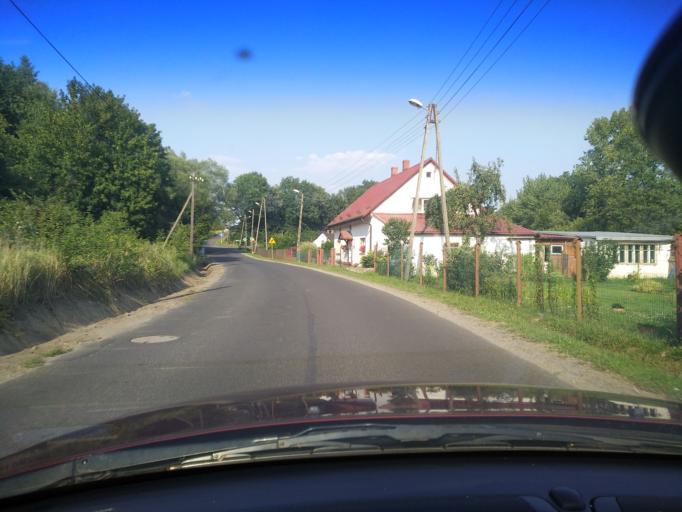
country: PL
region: Lower Silesian Voivodeship
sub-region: Powiat lubanski
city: Siekierczyn
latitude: 51.0863
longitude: 15.1376
